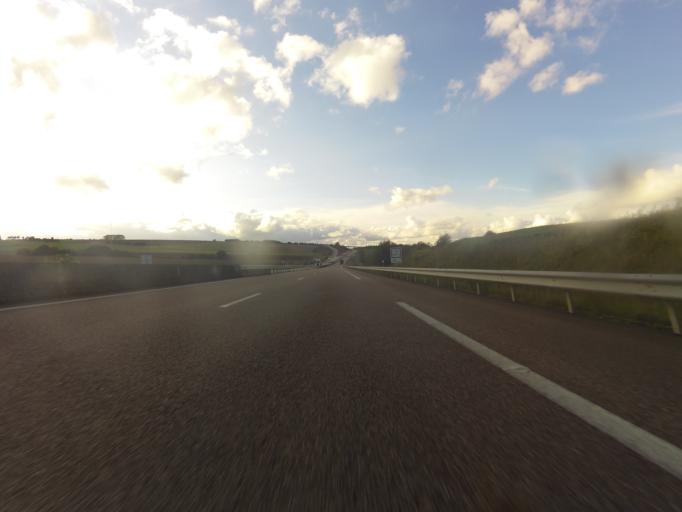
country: FR
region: Haute-Normandie
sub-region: Departement de la Seine-Maritime
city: Neufchatel-en-Bray
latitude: 49.7394
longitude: 1.5415
